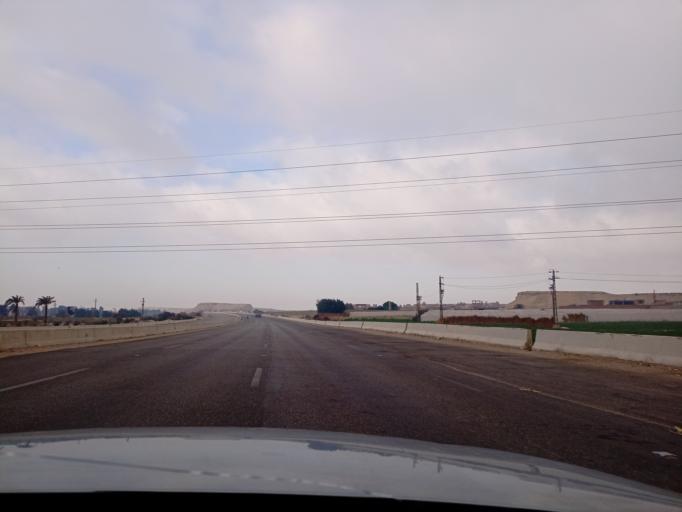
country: EG
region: Al Jizah
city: Al `Ayyat
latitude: 29.6827
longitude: 31.2221
